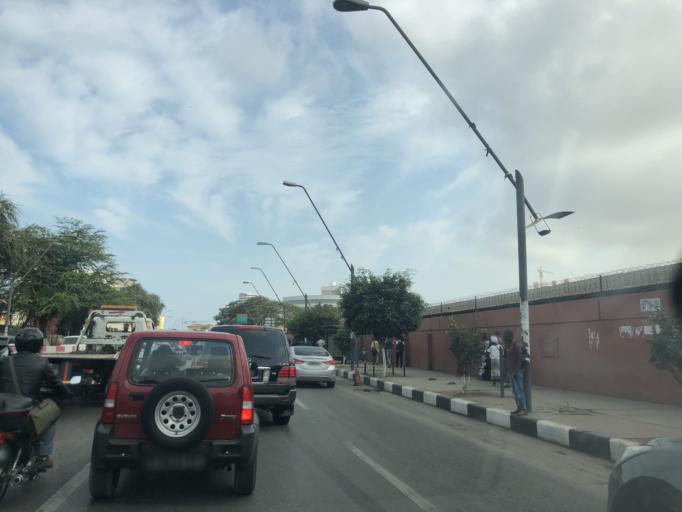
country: AO
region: Luanda
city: Luanda
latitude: -8.8428
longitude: 13.2329
